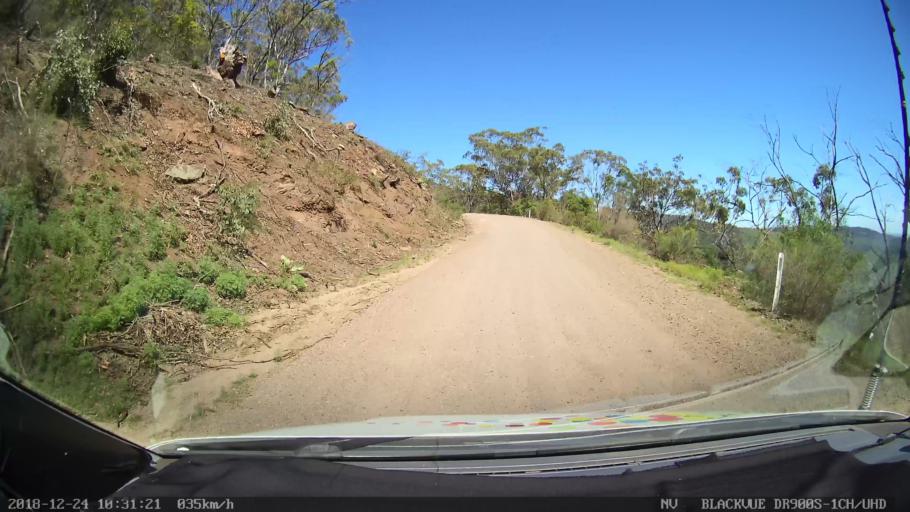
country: AU
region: New South Wales
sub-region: Upper Hunter Shire
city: Merriwa
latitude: -31.8392
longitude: 150.5225
